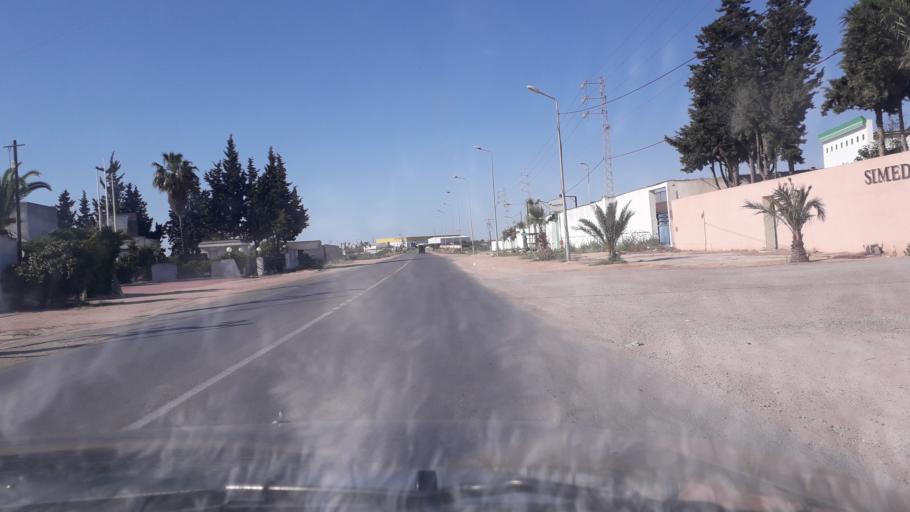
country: TN
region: Safaqis
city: Al Qarmadah
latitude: 34.8784
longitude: 10.7582
